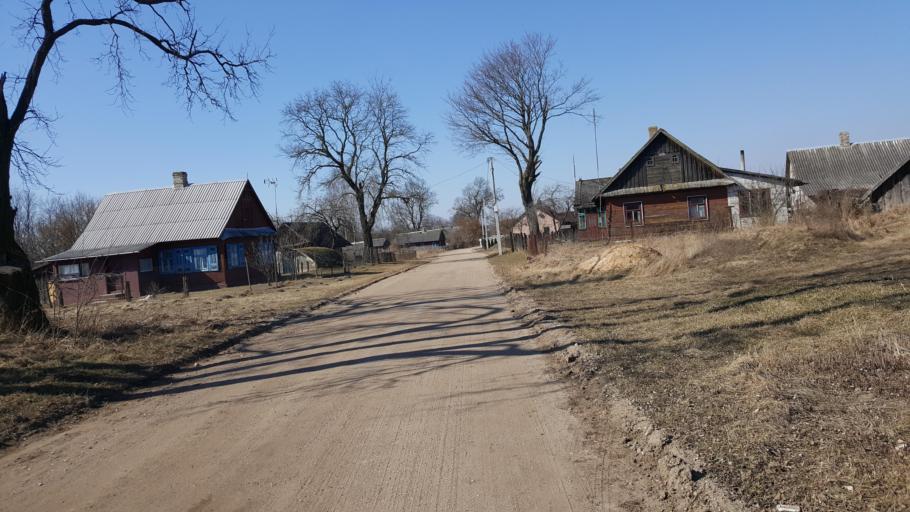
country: BY
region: Brest
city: Kamyanyets
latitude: 52.3711
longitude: 23.7892
